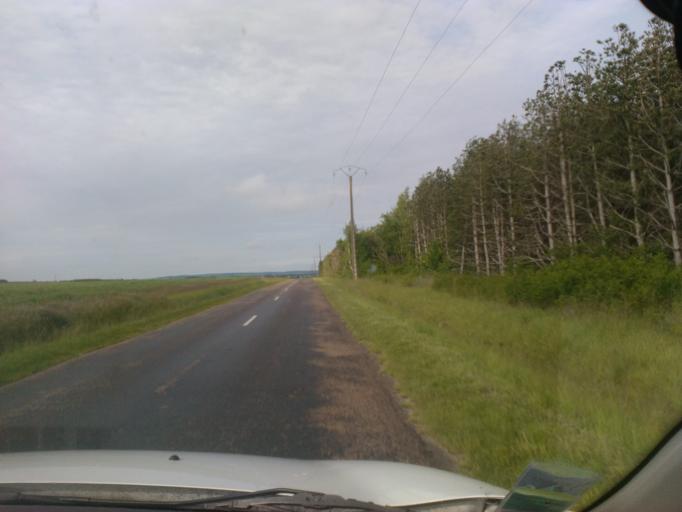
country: FR
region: Champagne-Ardenne
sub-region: Departement de l'Aube
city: Marigny-le-Chatel
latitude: 48.3906
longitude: 3.8078
